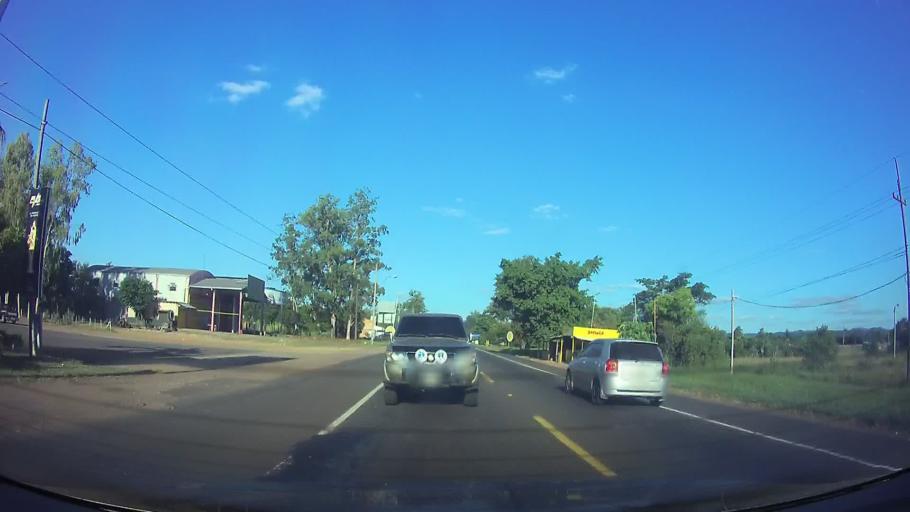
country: PY
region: Central
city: Ypacarai
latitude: -25.3805
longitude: -57.2486
